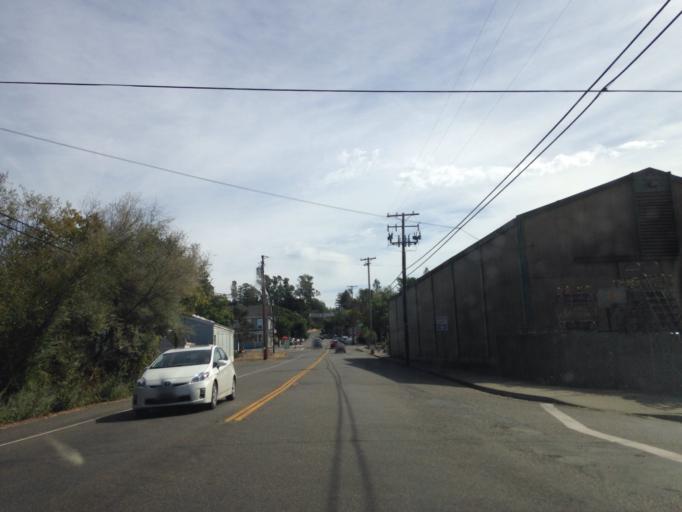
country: US
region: California
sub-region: Sonoma County
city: Graton
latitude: 38.4362
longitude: -122.8715
